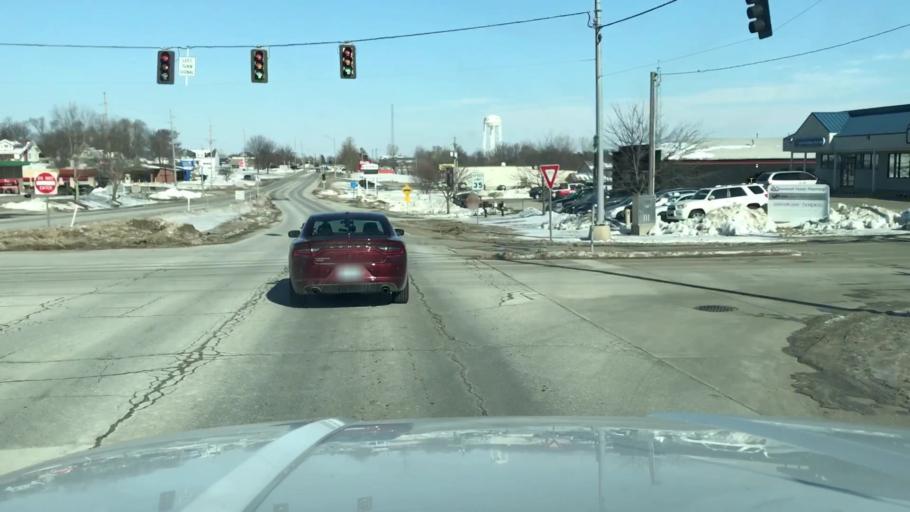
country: US
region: Missouri
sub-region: Andrew County
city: Savannah
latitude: 39.9391
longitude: -94.8217
